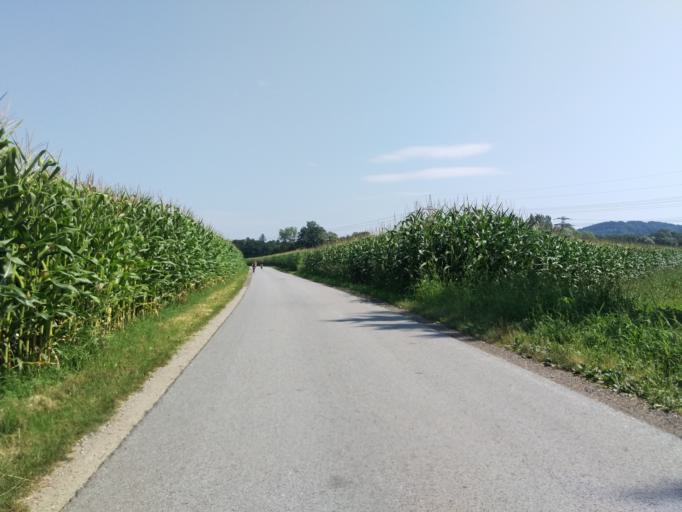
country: AT
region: Styria
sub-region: Politischer Bezirk Graz-Umgebung
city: Kalsdorf bei Graz
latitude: 46.9485
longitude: 15.4893
